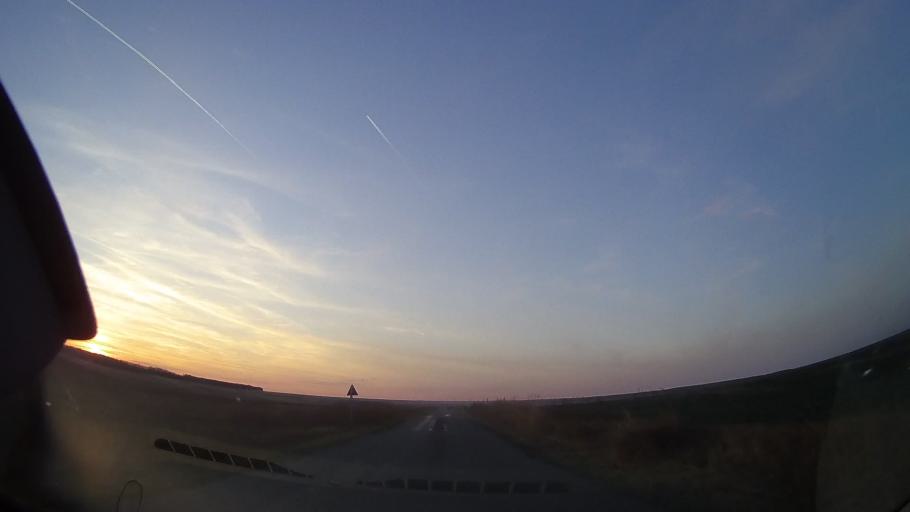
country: RO
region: Constanta
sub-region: Comuna Mereni
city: Mereni
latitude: 44.0161
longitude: 28.3086
